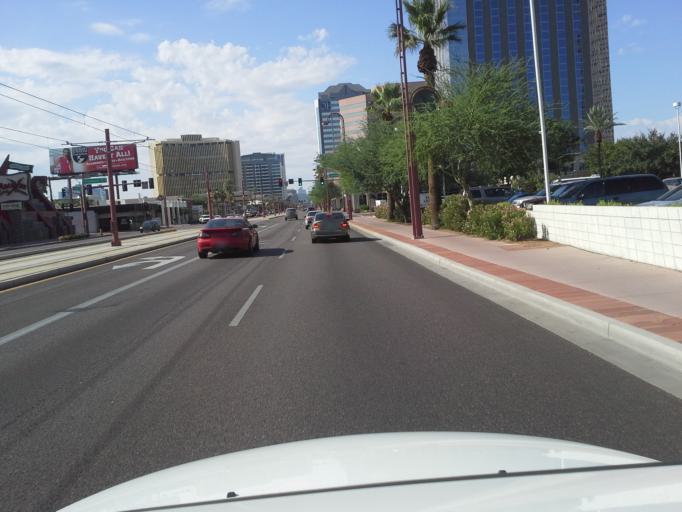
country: US
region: Arizona
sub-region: Maricopa County
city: Phoenix
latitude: 33.4933
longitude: -112.0740
